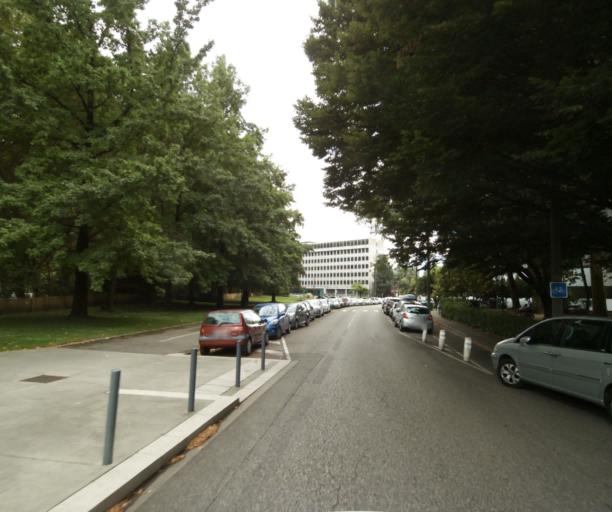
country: FR
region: Rhone-Alpes
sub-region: Departement de l'Isere
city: La Tronche
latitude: 45.1945
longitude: 5.7369
